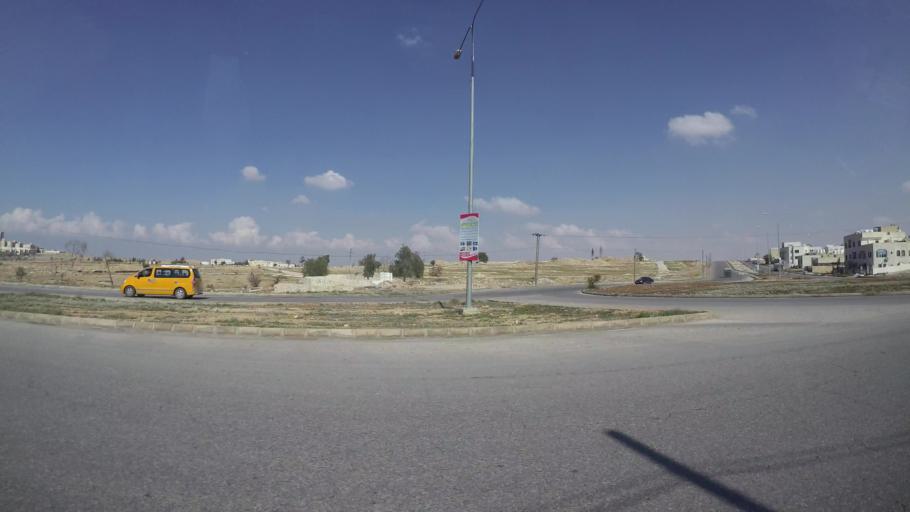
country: JO
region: Zarqa
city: Zarqa
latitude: 32.0629
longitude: 36.1123
